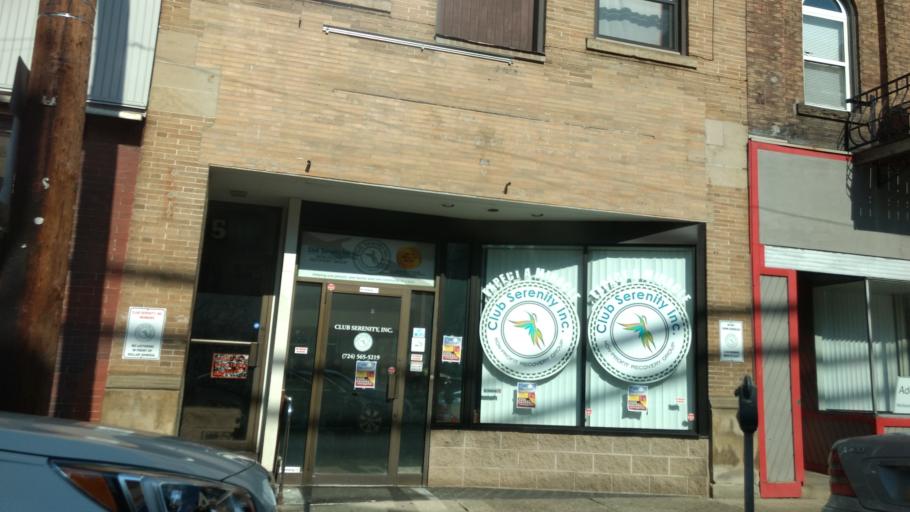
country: US
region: Pennsylvania
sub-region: Washington County
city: Charleroi
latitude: 40.1383
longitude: -79.8986
